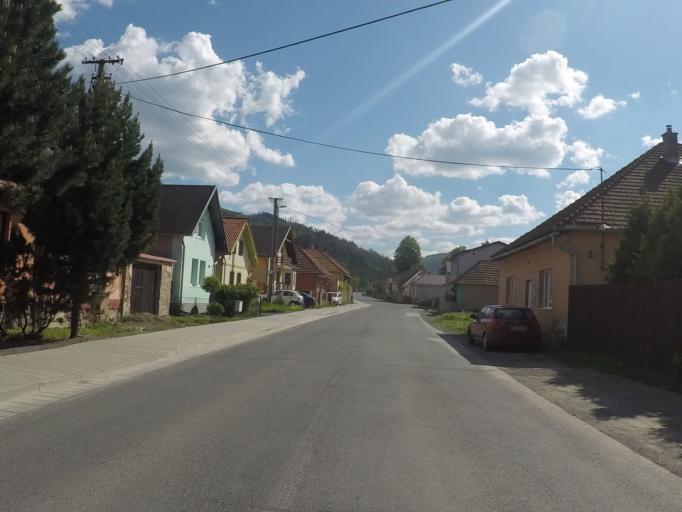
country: SK
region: Presovsky
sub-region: Okres Poprad
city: Poprad
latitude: 48.9860
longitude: 20.3072
